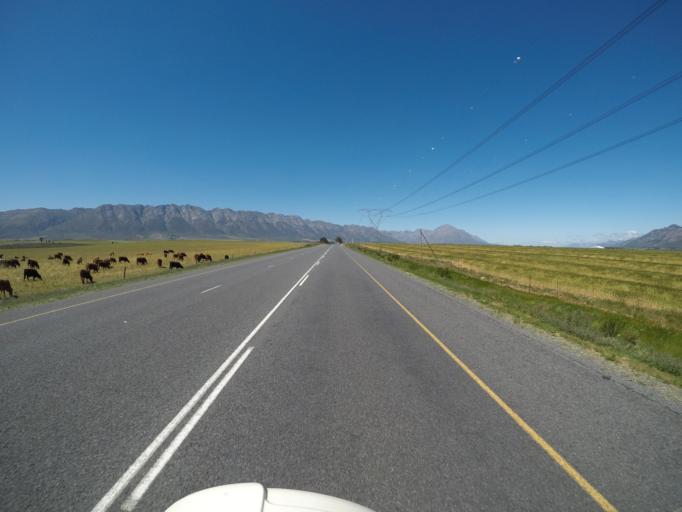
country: ZA
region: Western Cape
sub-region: Cape Winelands District Municipality
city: Ceres
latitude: -33.3156
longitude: 19.1288
